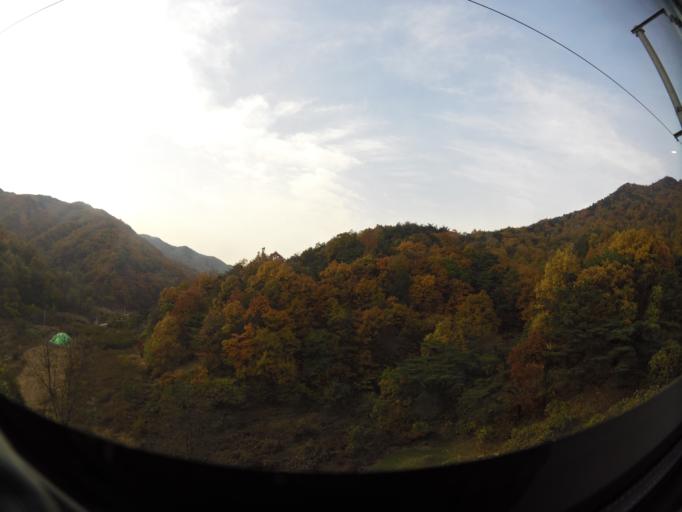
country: KR
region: Gyeongsangbuk-do
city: Gimcheon
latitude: 36.1661
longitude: 128.0064
